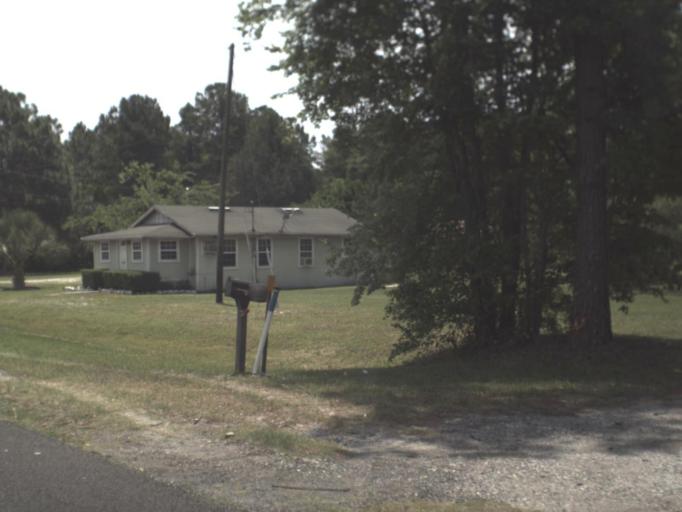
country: US
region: Florida
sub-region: Nassau County
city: Yulee
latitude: 30.6309
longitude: -81.5888
